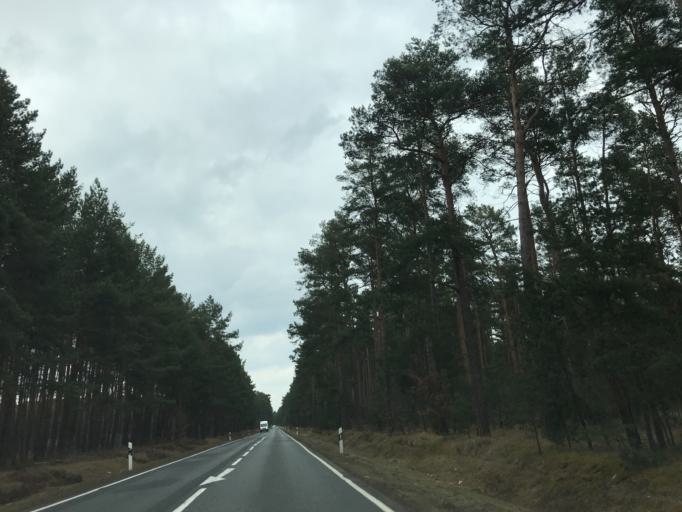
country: DE
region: Brandenburg
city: Fichtenwalde
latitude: 52.3004
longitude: 12.8636
